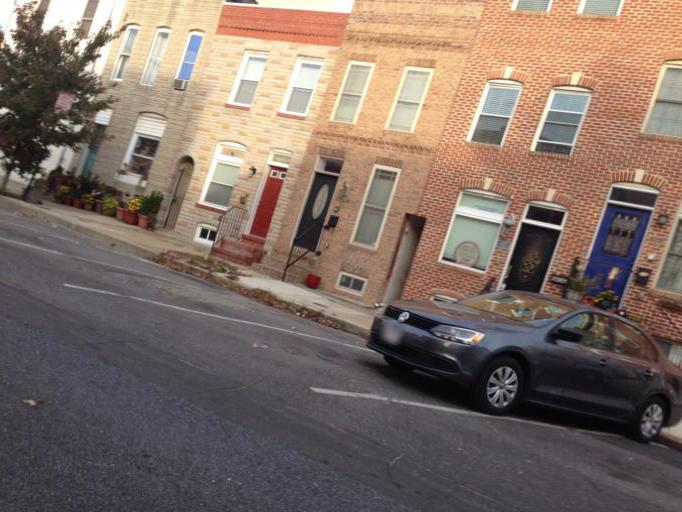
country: US
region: Maryland
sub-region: City of Baltimore
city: Baltimore
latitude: 39.2801
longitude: -76.5696
